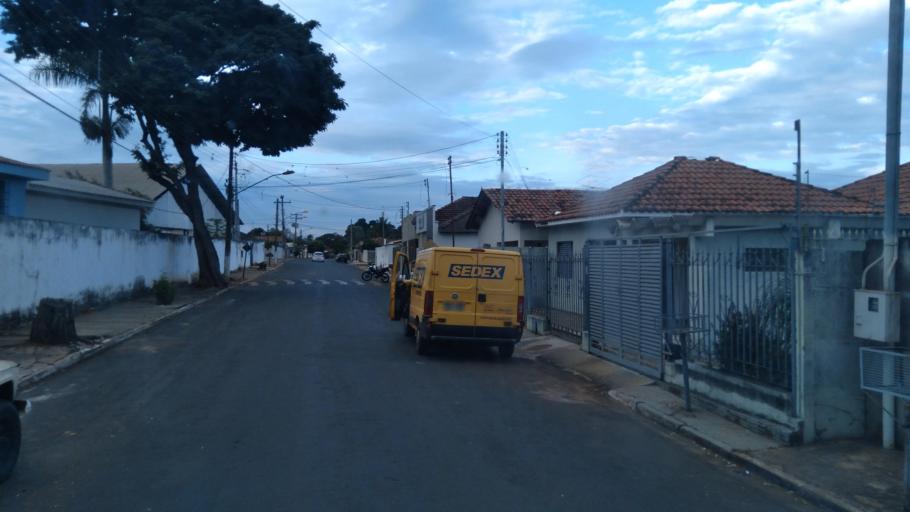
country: BR
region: Goias
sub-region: Mineiros
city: Mineiros
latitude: -17.5693
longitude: -52.5494
